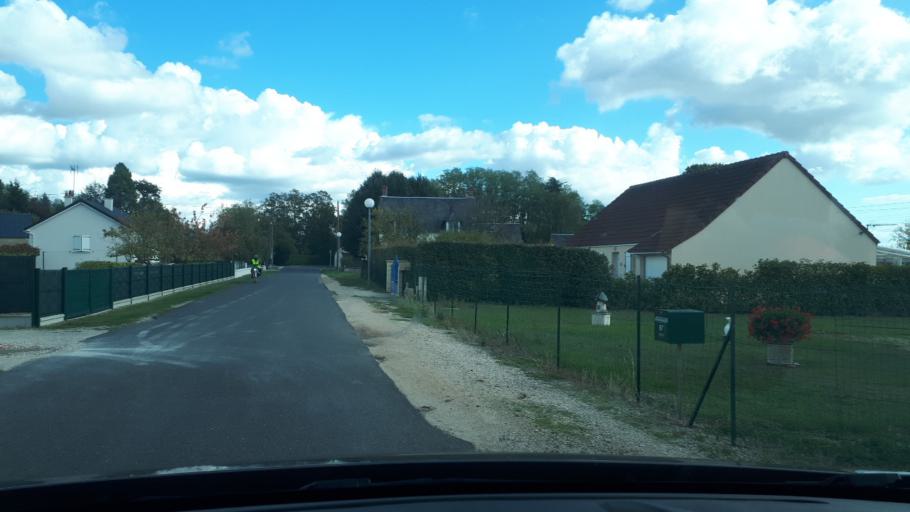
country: FR
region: Centre
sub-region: Departement du Loir-et-Cher
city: Saint-Aignan
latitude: 47.2916
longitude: 1.3753
